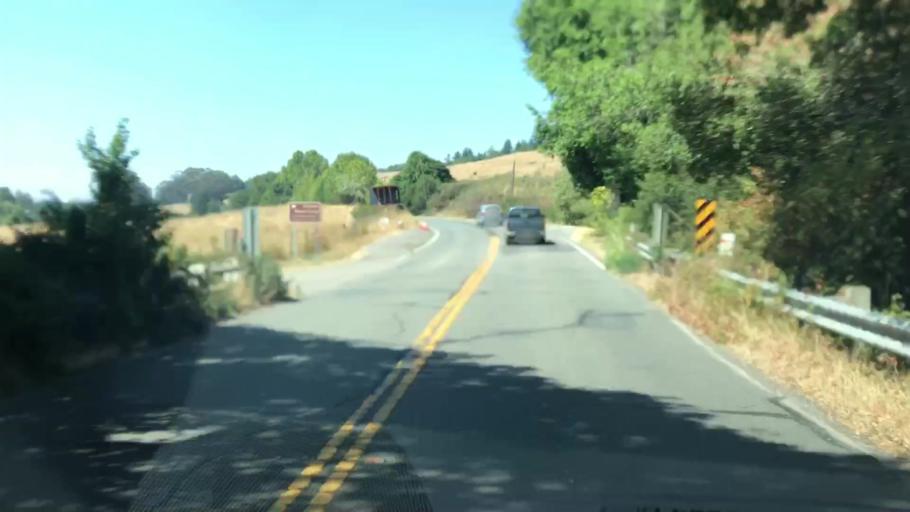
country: US
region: California
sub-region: Marin County
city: Lagunitas-Forest Knolls
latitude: 38.0024
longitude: -122.7588
